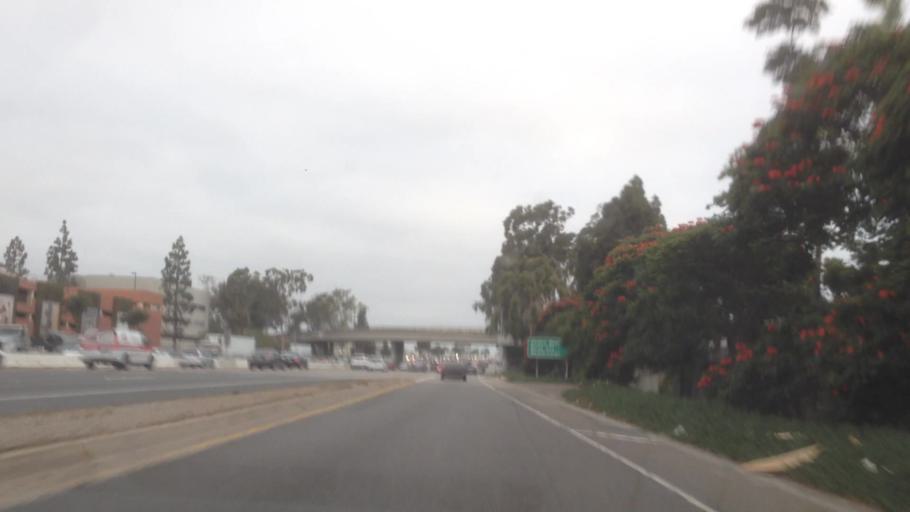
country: US
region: California
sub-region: Orange County
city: Midway City
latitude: 33.7356
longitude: -117.9931
